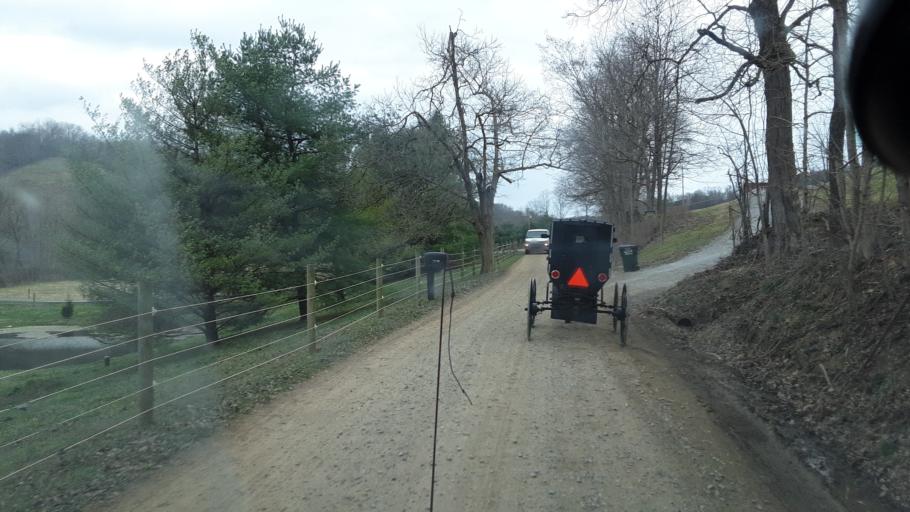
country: US
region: Ohio
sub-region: Coshocton County
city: West Lafayette
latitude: 40.3545
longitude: -81.7699
